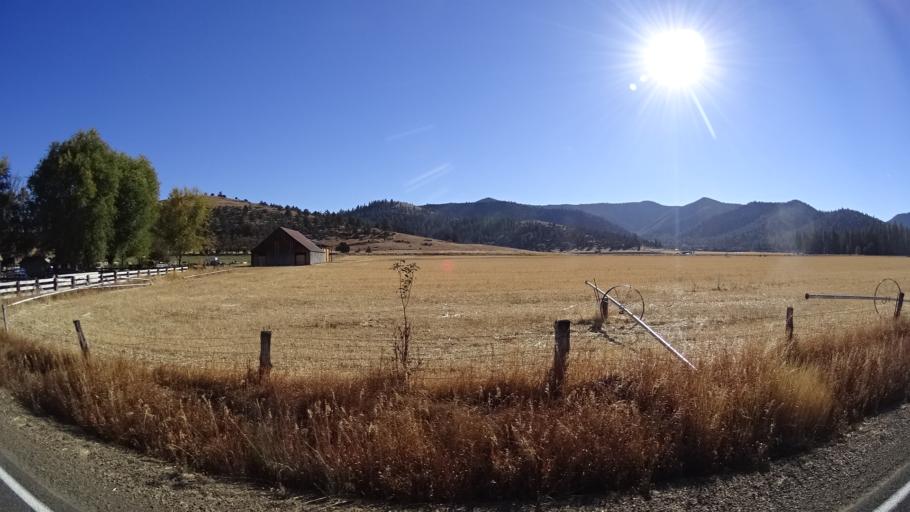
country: US
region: California
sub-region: Siskiyou County
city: Yreka
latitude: 41.5530
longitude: -122.8285
